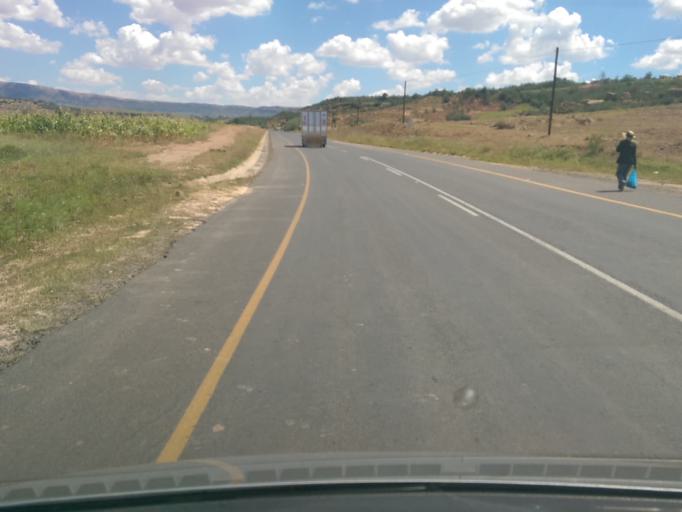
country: LS
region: Maseru
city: Maseru
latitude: -29.3930
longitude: 27.5432
